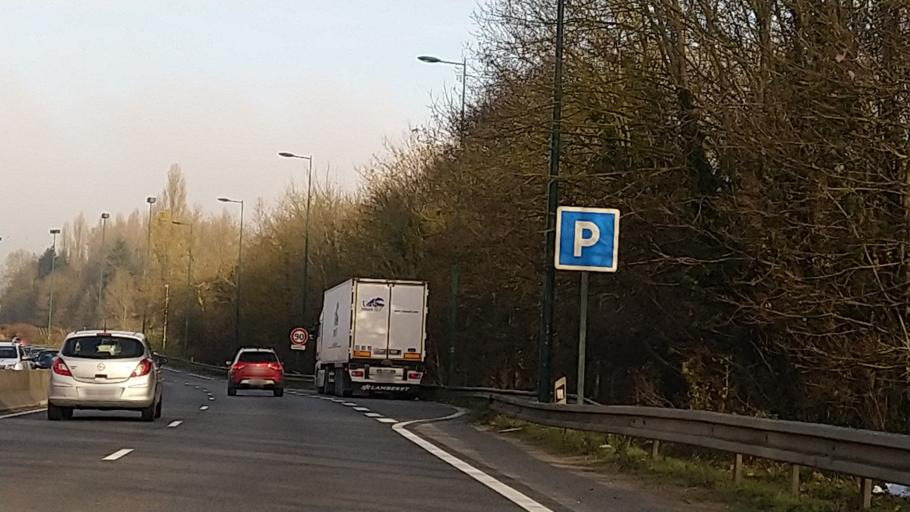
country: FR
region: Ile-de-France
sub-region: Departement du Val-d'Oise
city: Mours
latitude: 49.1324
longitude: 2.2561
